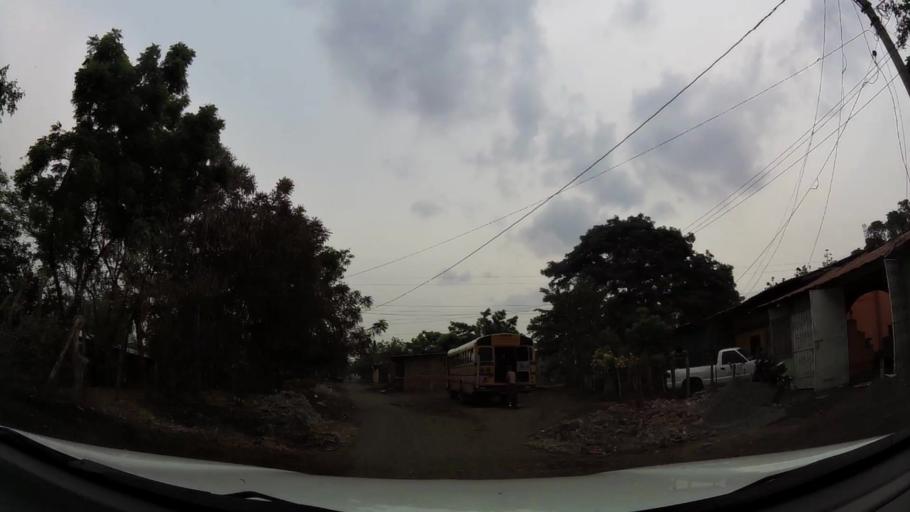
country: NI
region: Leon
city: Leon
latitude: 12.4514
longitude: -86.8660
